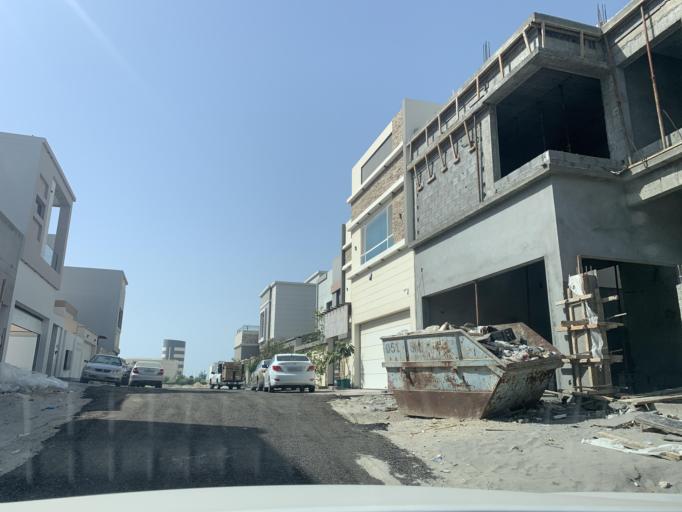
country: BH
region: Manama
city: Jidd Hafs
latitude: 26.2297
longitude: 50.4649
